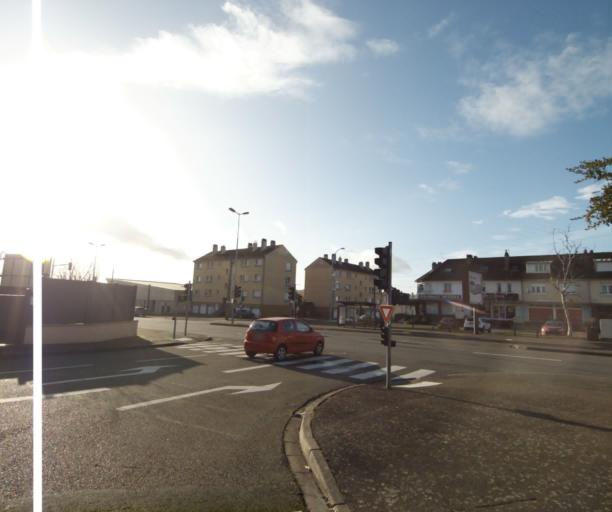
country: FR
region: Pays de la Loire
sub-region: Departement de la Sarthe
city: Le Mans
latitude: 47.9649
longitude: 0.2023
